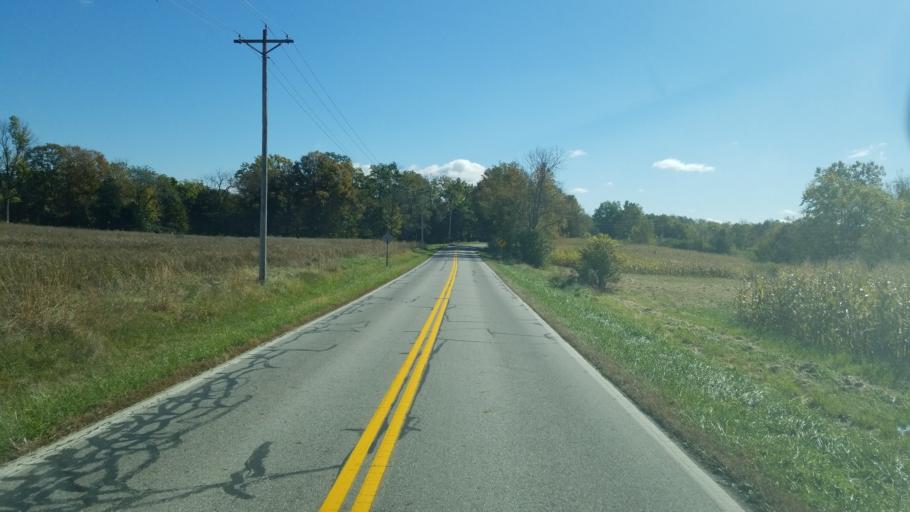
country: US
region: Ohio
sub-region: Highland County
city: Leesburg
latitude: 39.2752
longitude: -83.4861
